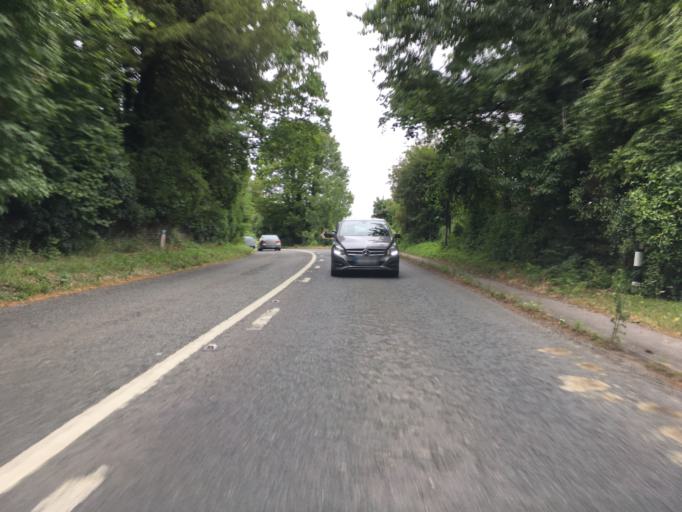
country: GB
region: England
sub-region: Gloucestershire
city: Charlton Kings
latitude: 51.8788
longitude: -2.0317
